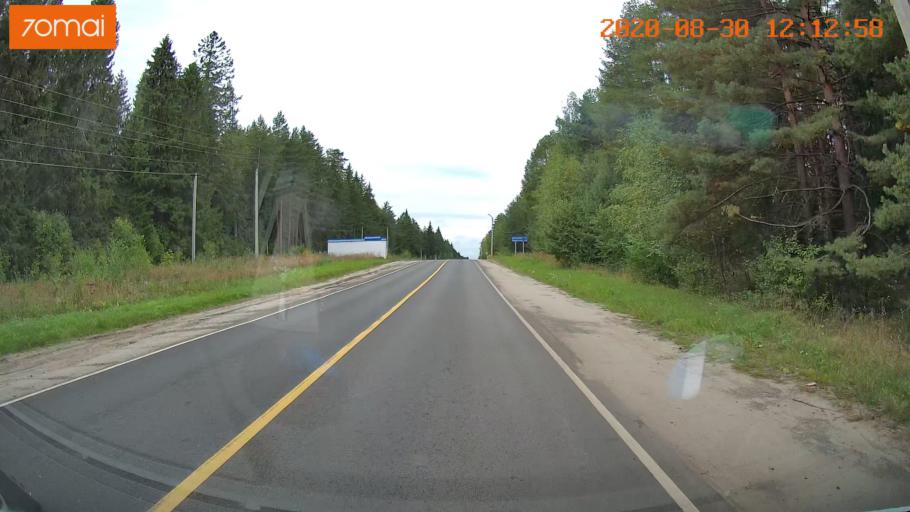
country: RU
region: Ivanovo
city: Yur'yevets
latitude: 57.3119
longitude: 43.0877
